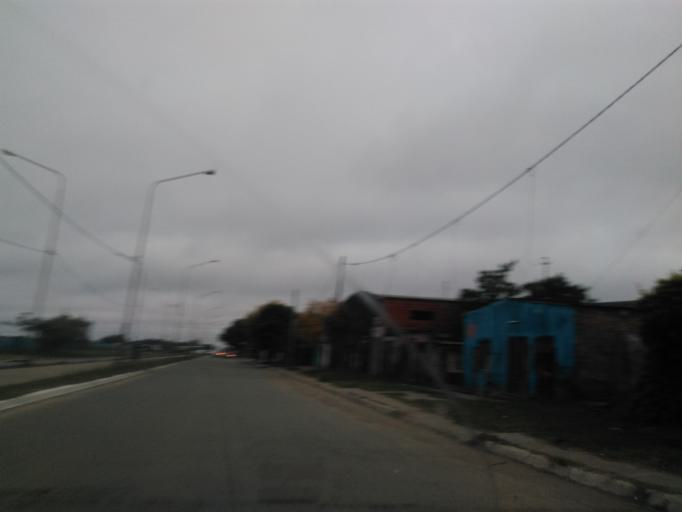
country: AR
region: Chaco
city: Resistencia
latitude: -27.4816
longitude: -58.9920
